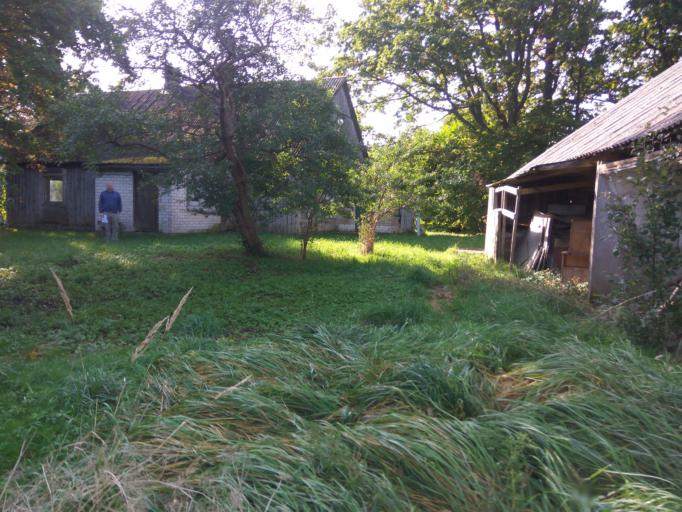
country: LV
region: Ventspils
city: Ventspils
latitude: 57.3564
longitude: 21.6638
